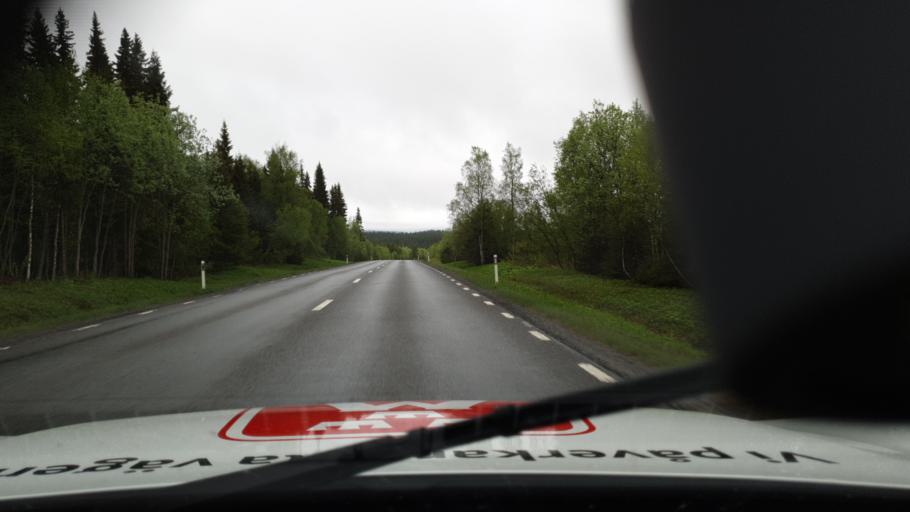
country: SE
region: Jaemtland
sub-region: OEstersunds Kommun
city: Lit
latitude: 63.4644
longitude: 15.1850
